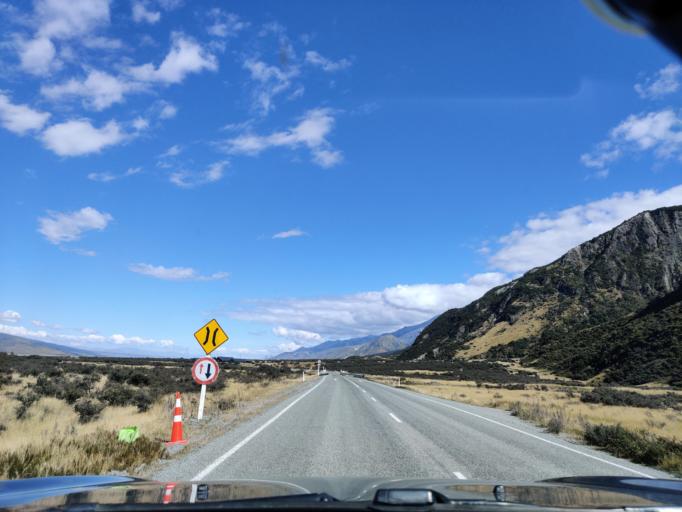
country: NZ
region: Canterbury
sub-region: Timaru District
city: Pleasant Point
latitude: -43.7540
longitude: 170.1176
